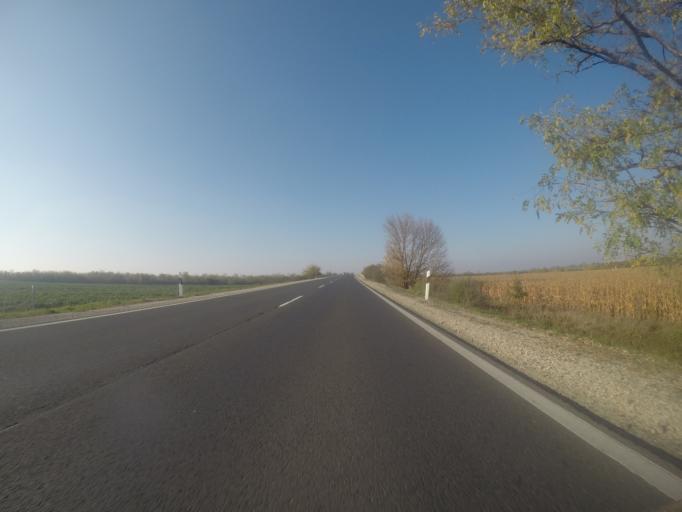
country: HU
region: Fejer
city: Ercsi
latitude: 47.2733
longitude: 18.8798
